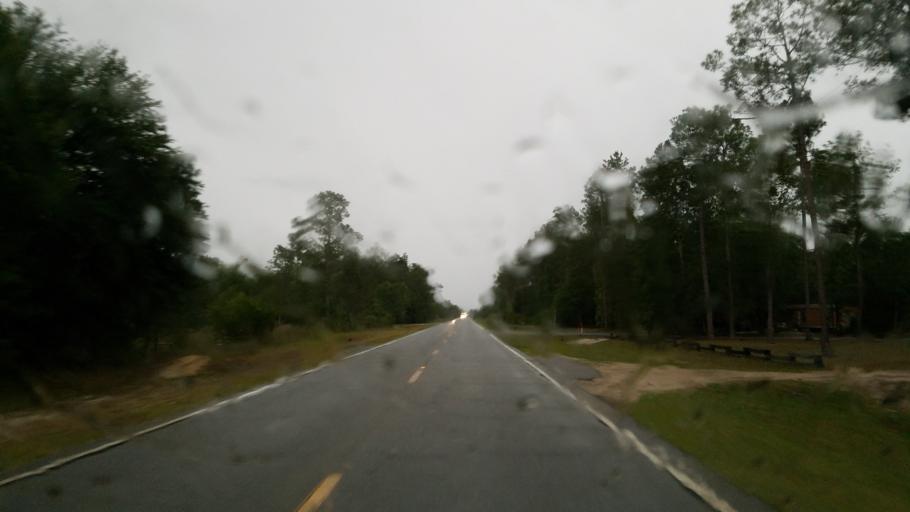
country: US
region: Georgia
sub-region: Lanier County
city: Lakeland
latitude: 30.9075
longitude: -83.0075
